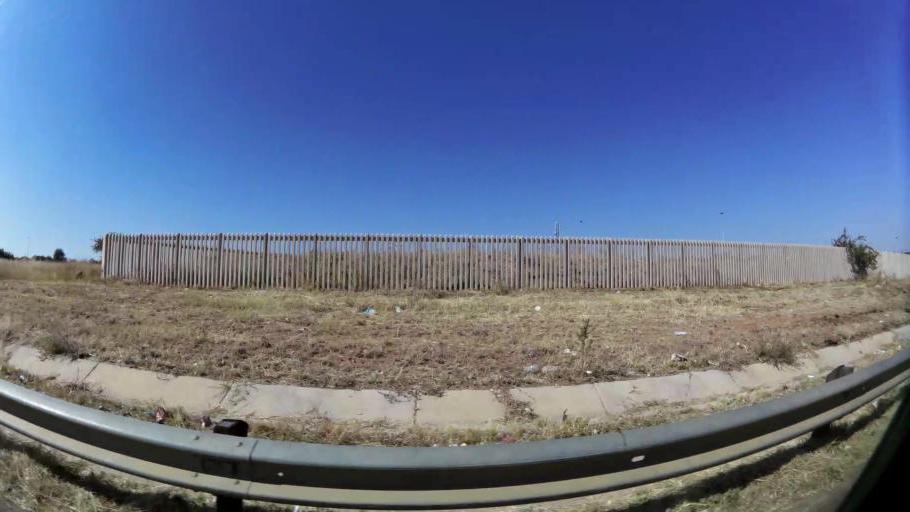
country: ZA
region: Gauteng
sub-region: City of Tshwane Metropolitan Municipality
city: Mabopane
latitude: -25.5271
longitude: 28.0858
